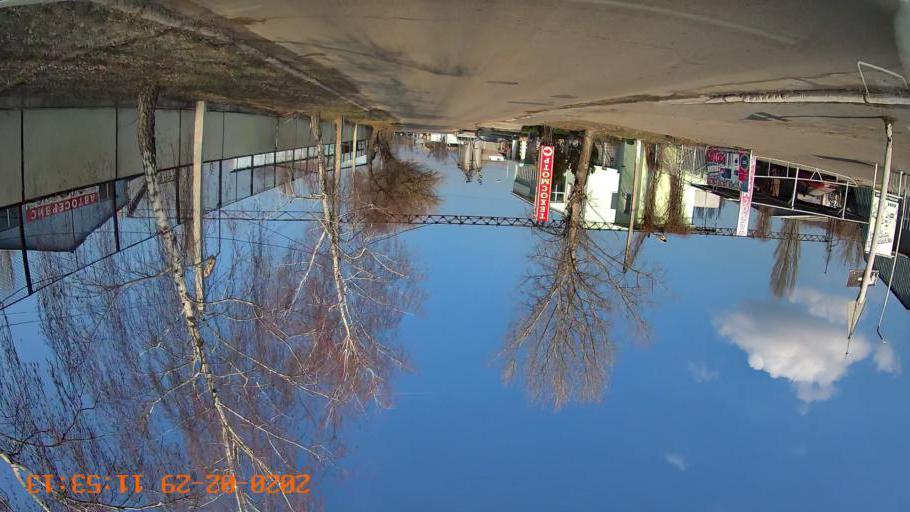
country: MD
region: Telenesti
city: Ribnita
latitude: 47.7756
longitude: 28.9907
